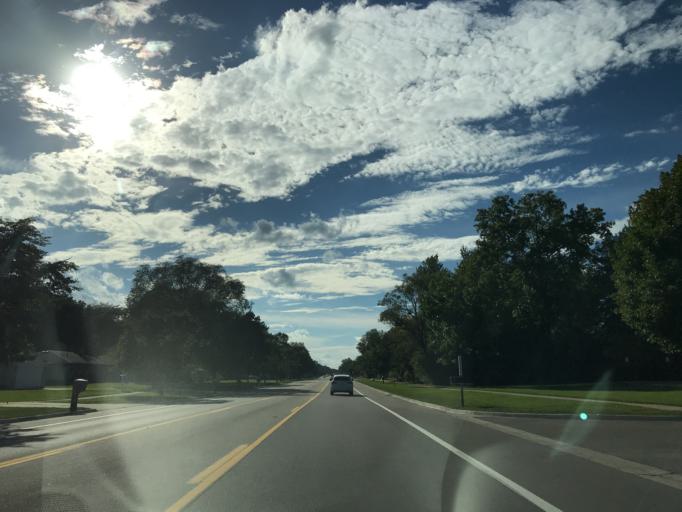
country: US
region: Michigan
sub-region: Oakland County
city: Farmington Hills
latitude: 42.5135
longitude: -83.3693
